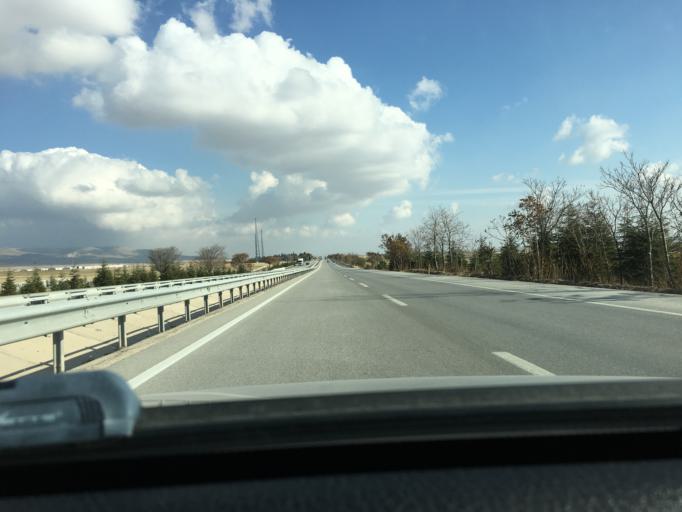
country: TR
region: Eskisehir
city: Kaymaz
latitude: 39.4786
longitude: 31.3104
